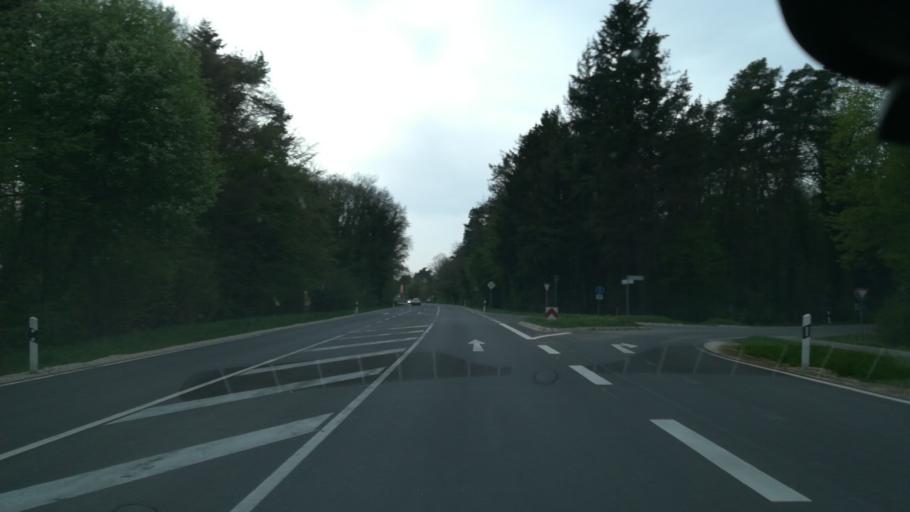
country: DE
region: Baden-Wuerttemberg
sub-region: Freiburg Region
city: Moos
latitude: 47.7600
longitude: 8.8987
